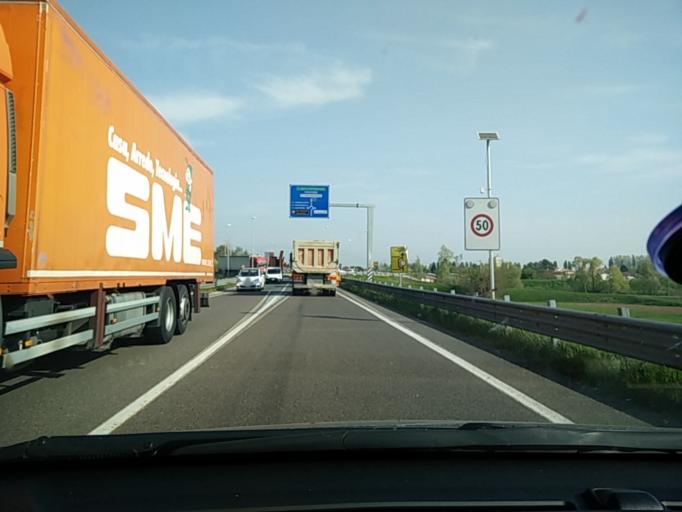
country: IT
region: Veneto
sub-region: Provincia di Treviso
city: Portobuffole
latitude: 45.8487
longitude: 12.5367
